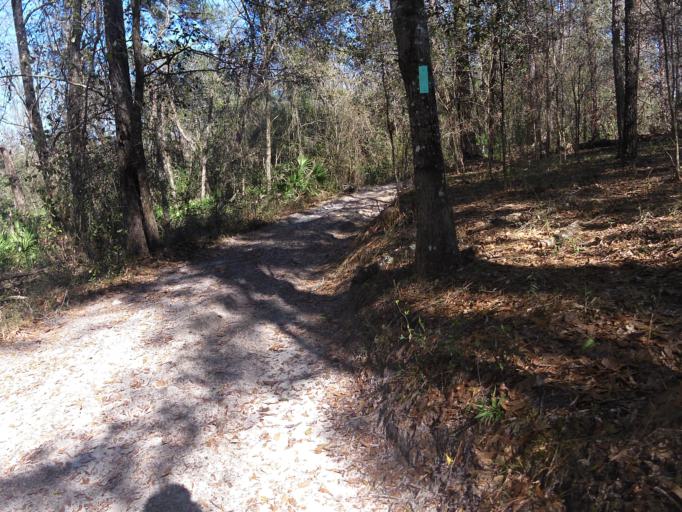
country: US
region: Florida
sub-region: Clay County
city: Middleburg
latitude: 30.1374
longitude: -81.8883
